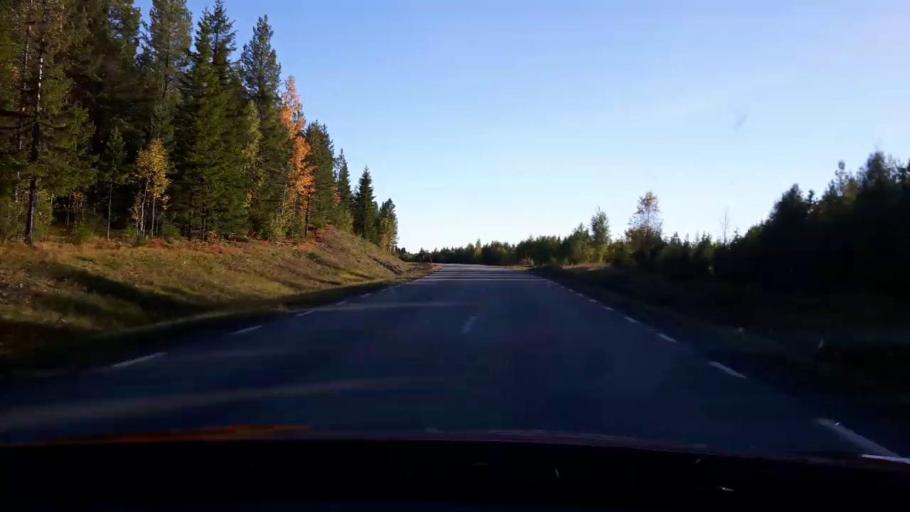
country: SE
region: Jaemtland
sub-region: OEstersunds Kommun
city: Lit
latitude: 63.7578
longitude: 14.7170
